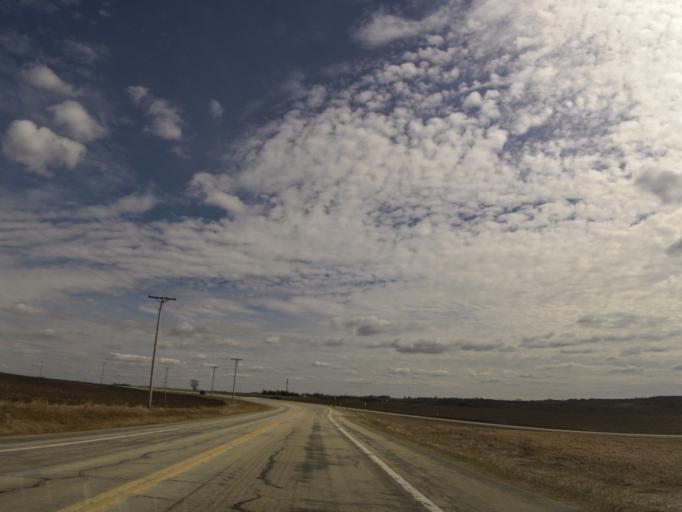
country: US
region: Minnesota
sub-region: Olmsted County
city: Rochester
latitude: 43.9583
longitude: -92.4272
